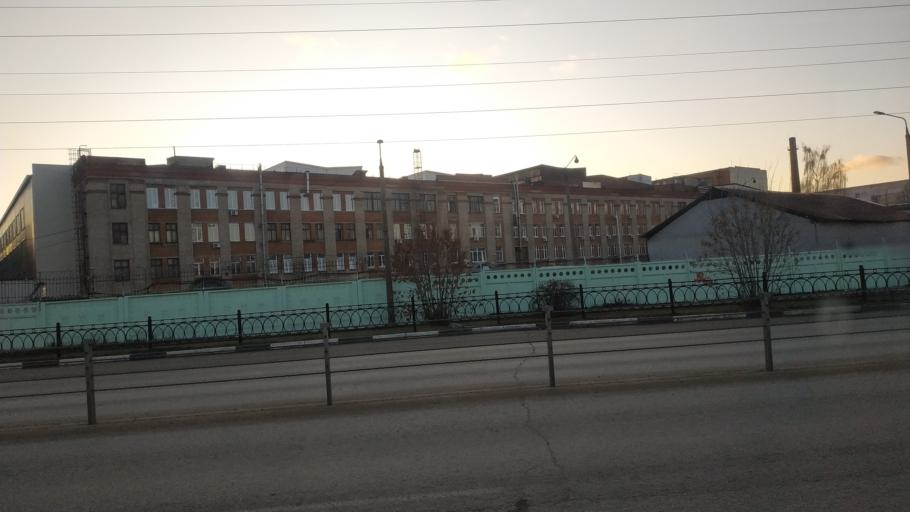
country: RU
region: Moskovskaya
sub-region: Podol'skiy Rayon
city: Podol'sk
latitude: 55.4148
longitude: 37.5787
